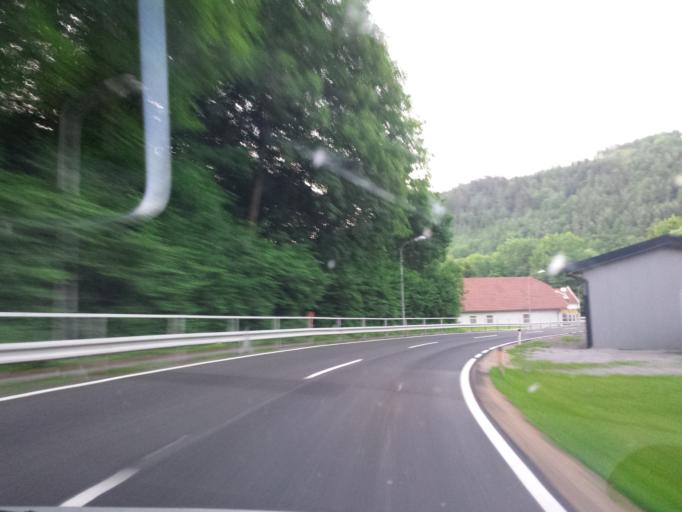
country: AT
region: Lower Austria
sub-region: Politischer Bezirk Lilienfeld
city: Hainfeld
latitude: 48.0237
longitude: 15.7747
